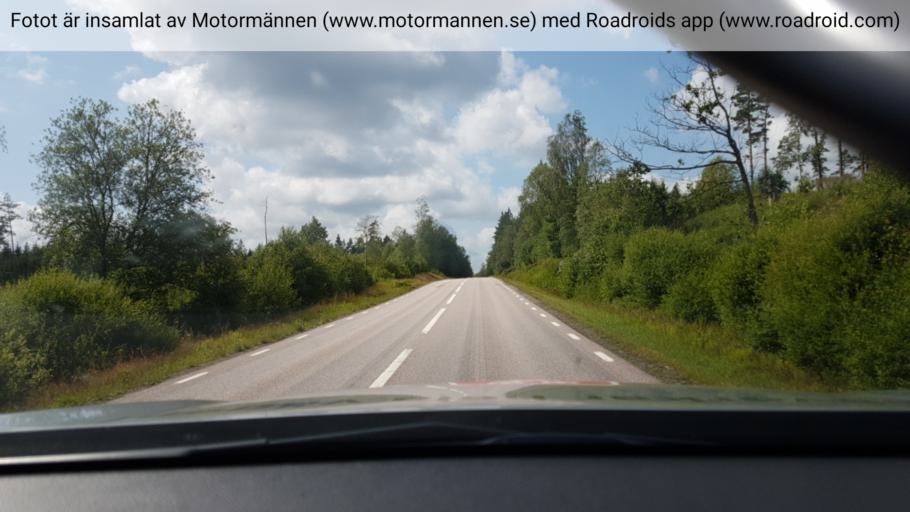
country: SE
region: Vaestra Goetaland
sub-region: Svenljunga Kommun
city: Svenljunga
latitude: 57.4887
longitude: 12.9909
